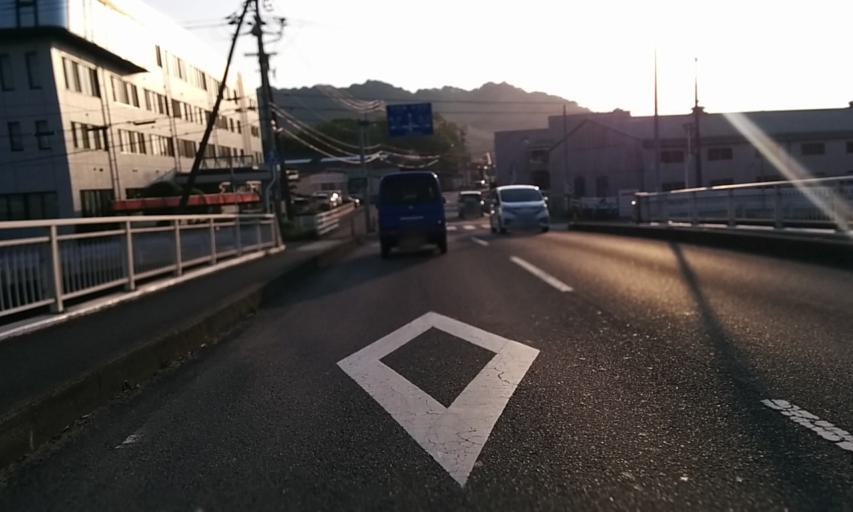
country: JP
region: Ehime
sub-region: Shikoku-chuo Shi
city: Matsuyama
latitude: 33.7816
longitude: 132.7911
